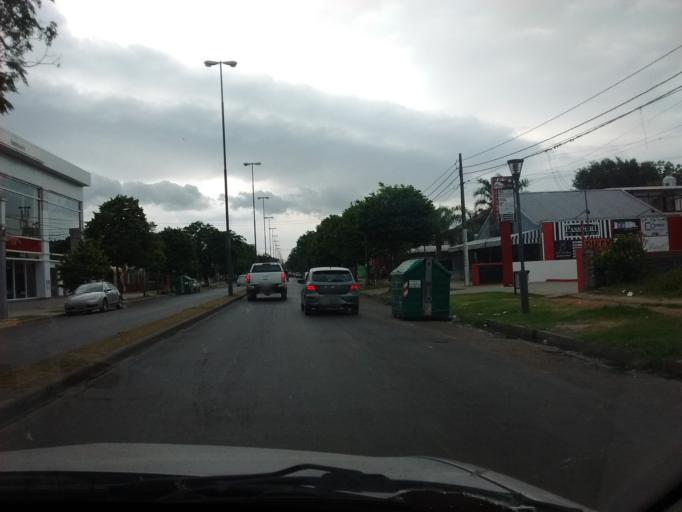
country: AR
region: Santa Fe
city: Granadero Baigorria
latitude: -32.9300
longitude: -60.7298
